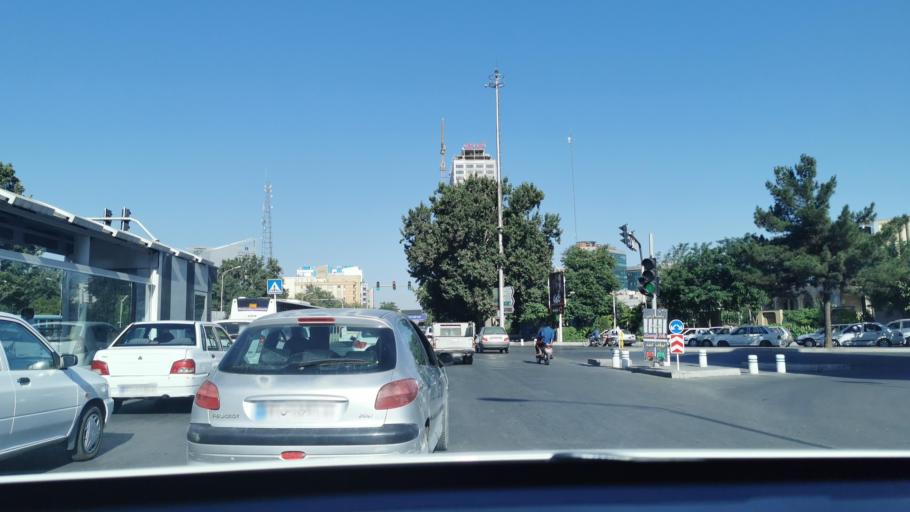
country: IR
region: Razavi Khorasan
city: Mashhad
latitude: 36.3242
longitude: 59.5707
